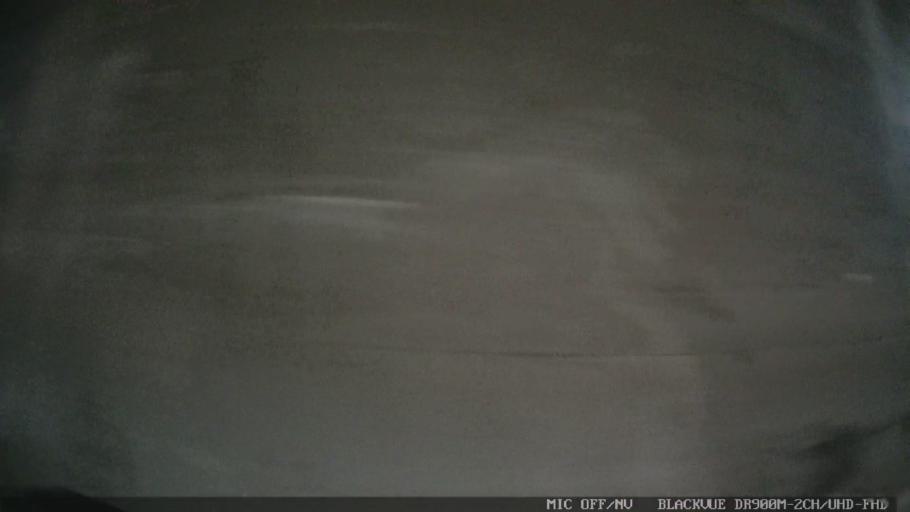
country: BR
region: Sao Paulo
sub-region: Cubatao
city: Cubatao
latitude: -23.9154
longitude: -46.5287
